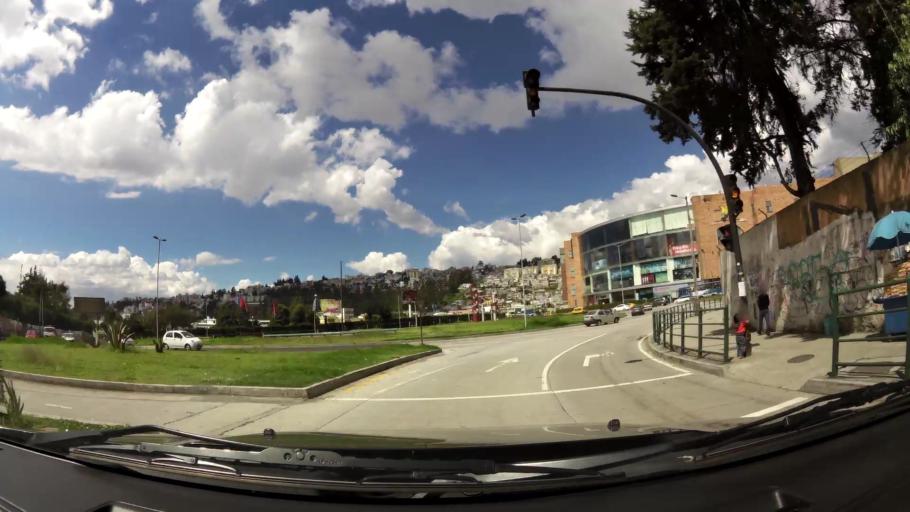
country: EC
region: Pichincha
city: Quito
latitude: -0.1022
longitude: -78.4916
